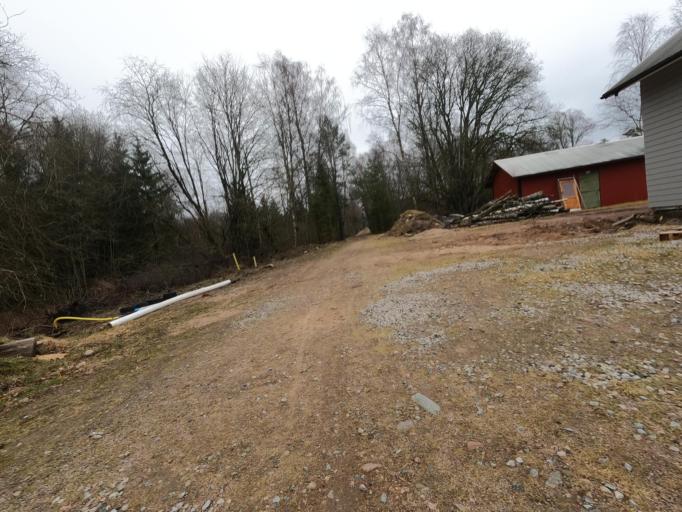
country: SE
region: Kronoberg
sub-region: Markaryds Kommun
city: Stromsnasbruk
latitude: 56.7911
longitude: 13.5693
